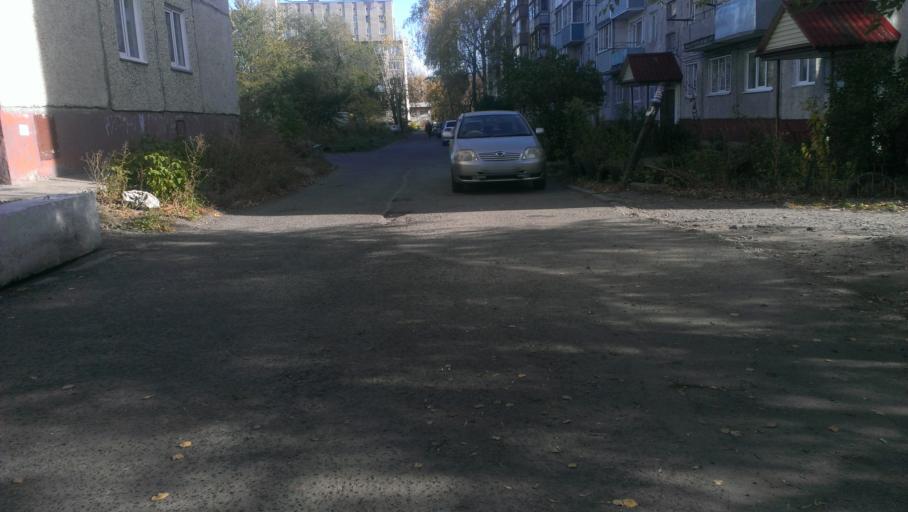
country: RU
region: Altai Krai
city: Novosilikatnyy
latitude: 53.3513
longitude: 83.6839
